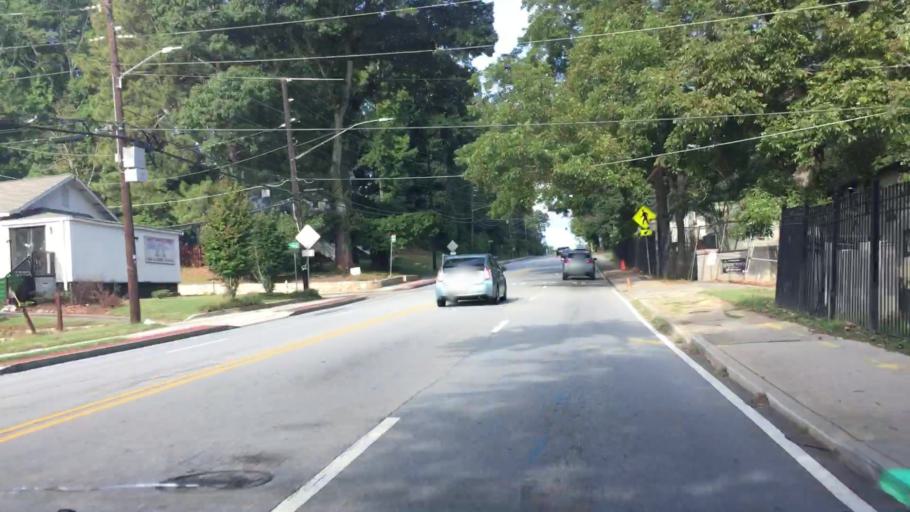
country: US
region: Georgia
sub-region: DeKalb County
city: Druid Hills
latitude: 33.7476
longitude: -84.3381
